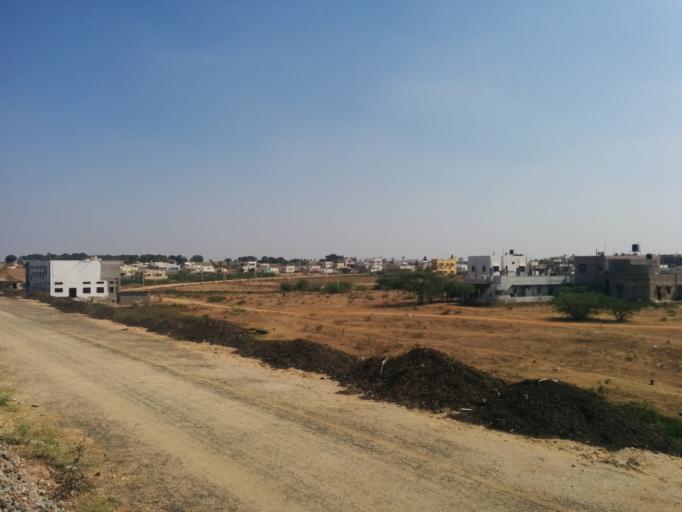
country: IN
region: Karnataka
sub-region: Gadag
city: Gadag
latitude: 15.4377
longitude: 75.6555
